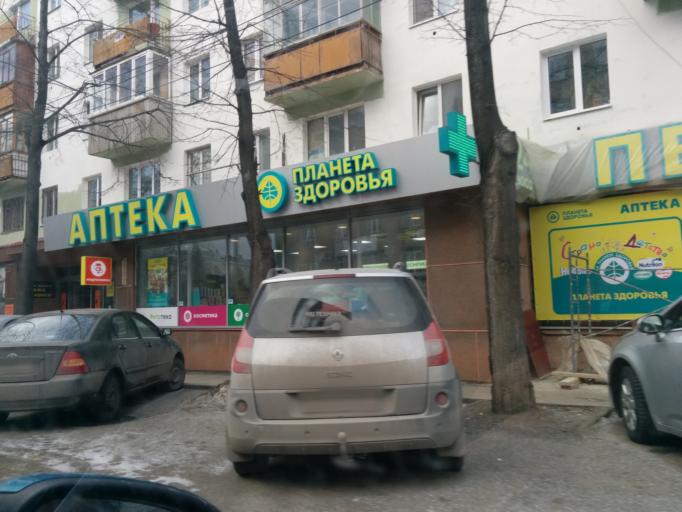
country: RU
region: Perm
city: Perm
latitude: 58.0098
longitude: 56.2423
